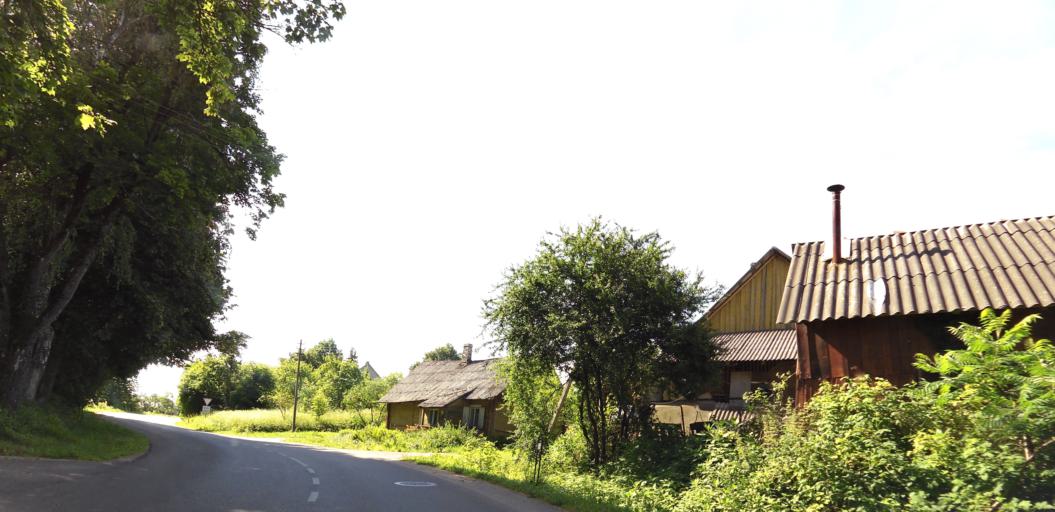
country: LT
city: Grigiskes
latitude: 54.7815
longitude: 25.0872
